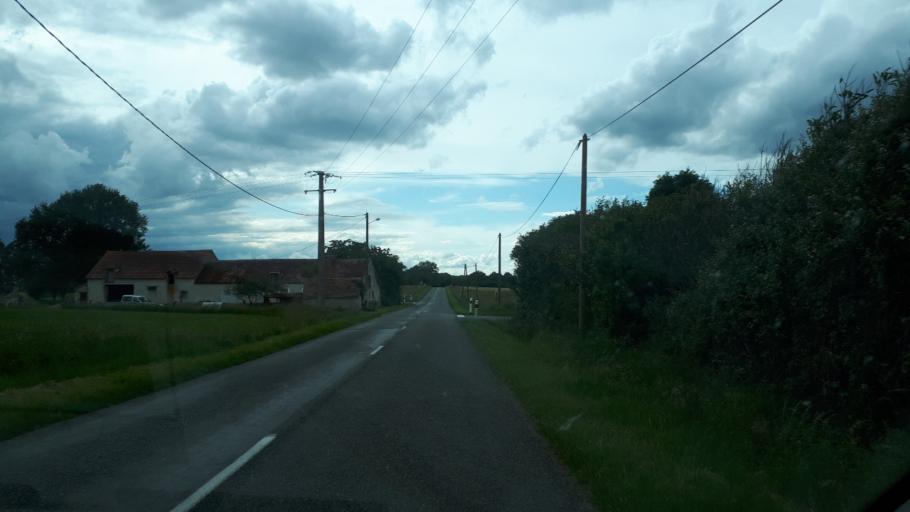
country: FR
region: Centre
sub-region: Departement du Cher
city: Gracay
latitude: 47.1770
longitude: 1.8154
